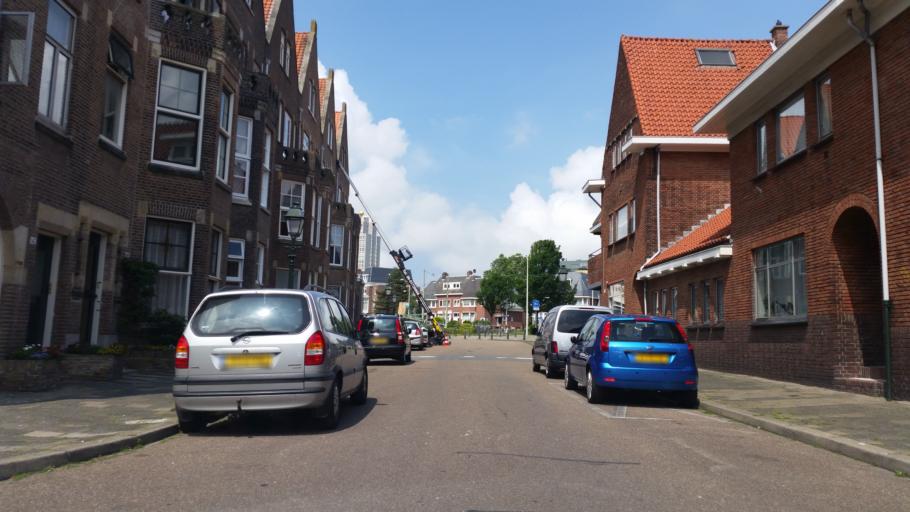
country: NL
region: South Holland
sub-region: Gemeente Den Haag
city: Scheveningen
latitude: 52.1094
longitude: 4.2840
